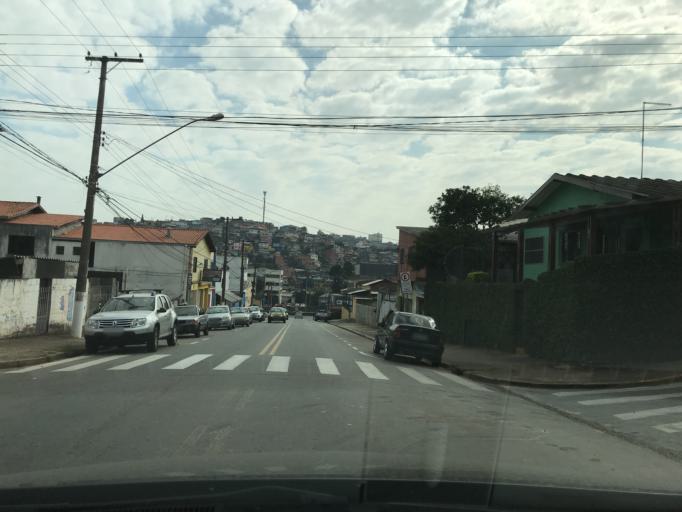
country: BR
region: Sao Paulo
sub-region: Cotia
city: Cotia
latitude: -23.6041
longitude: -46.9102
